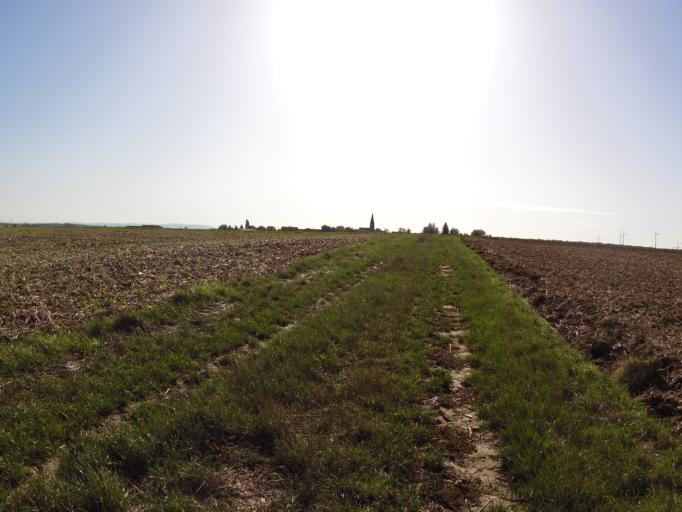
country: DE
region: Bavaria
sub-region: Regierungsbezirk Unterfranken
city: Theilheim
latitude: 49.7506
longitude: 10.0597
